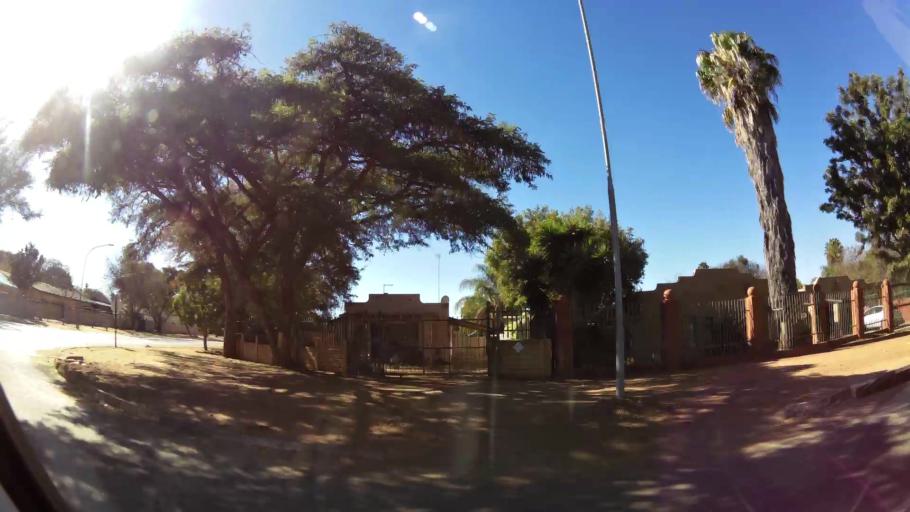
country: ZA
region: Limpopo
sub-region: Capricorn District Municipality
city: Polokwane
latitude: -23.9113
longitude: 29.4779
